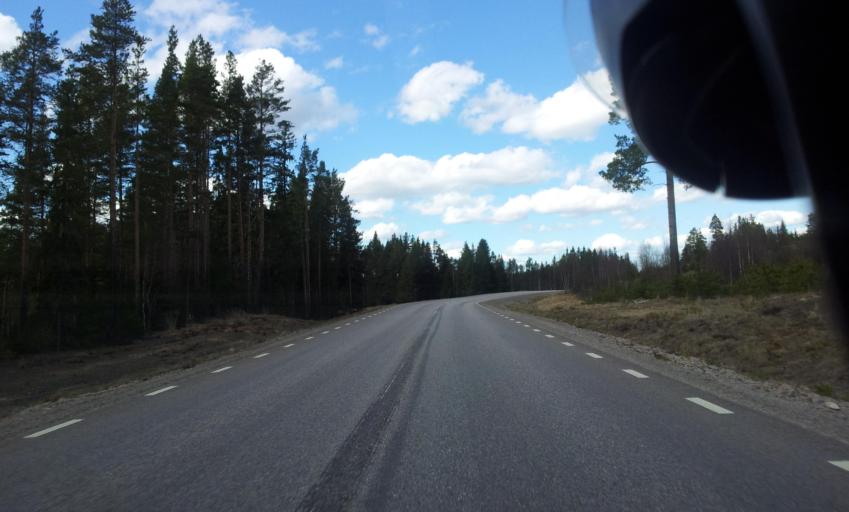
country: SE
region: Gaevleborg
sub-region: Ovanakers Kommun
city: Edsbyn
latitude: 61.1854
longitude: 15.8772
